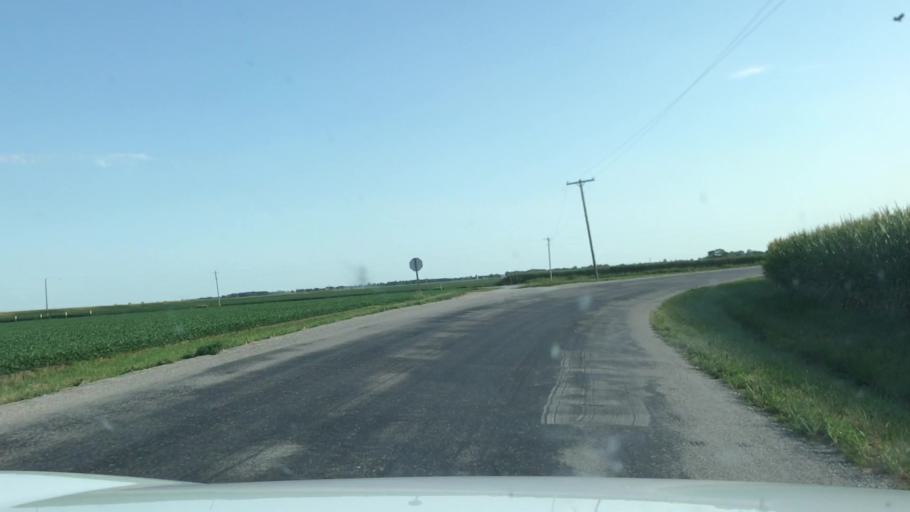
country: US
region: Illinois
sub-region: Washington County
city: Okawville
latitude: 38.4142
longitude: -89.4777
